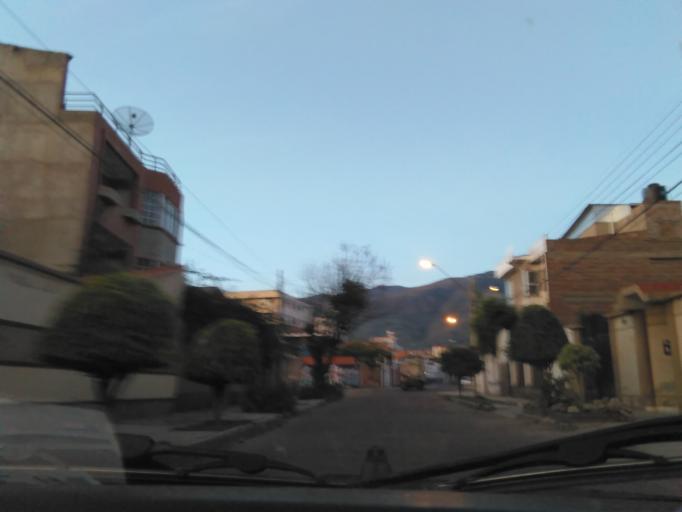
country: BO
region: Cochabamba
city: Cochabamba
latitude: -17.3740
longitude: -66.1661
